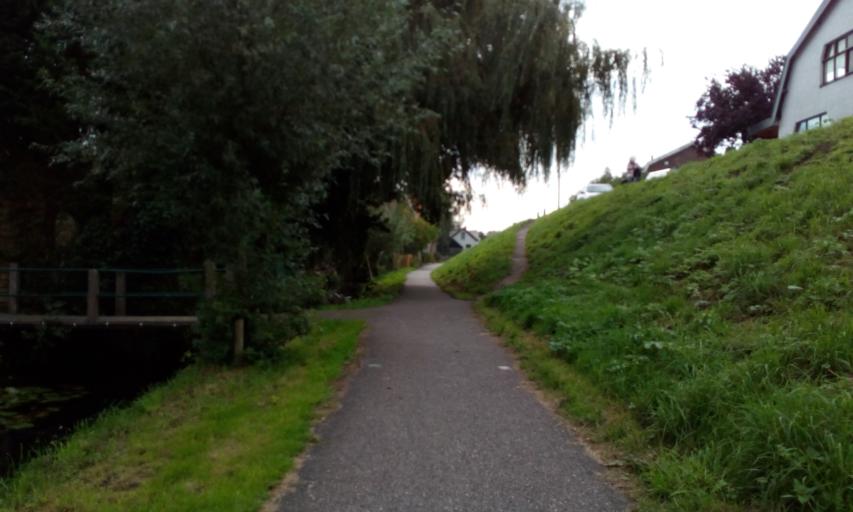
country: NL
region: South Holland
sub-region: Gemeente Albrandswaard
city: Rhoon
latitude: 51.8530
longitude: 4.3945
